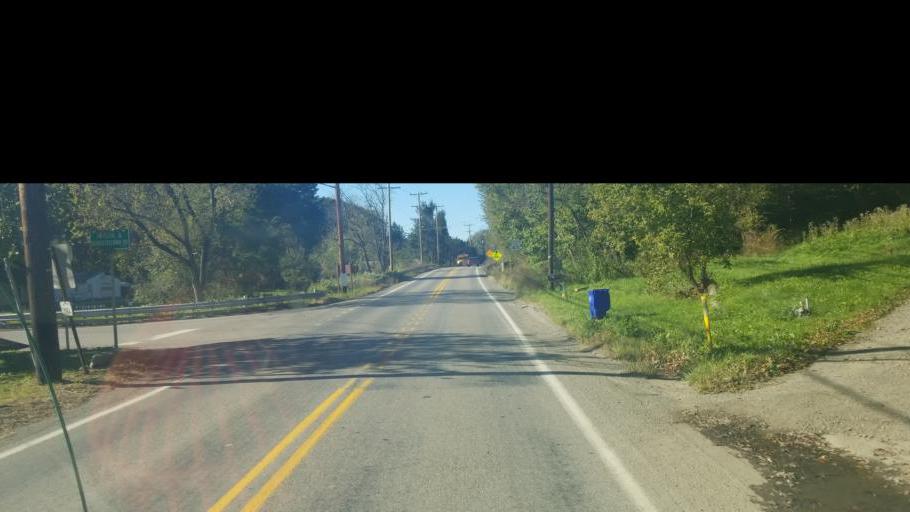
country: US
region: Pennsylvania
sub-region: Allegheny County
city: Imperial
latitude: 40.4546
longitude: -80.2550
